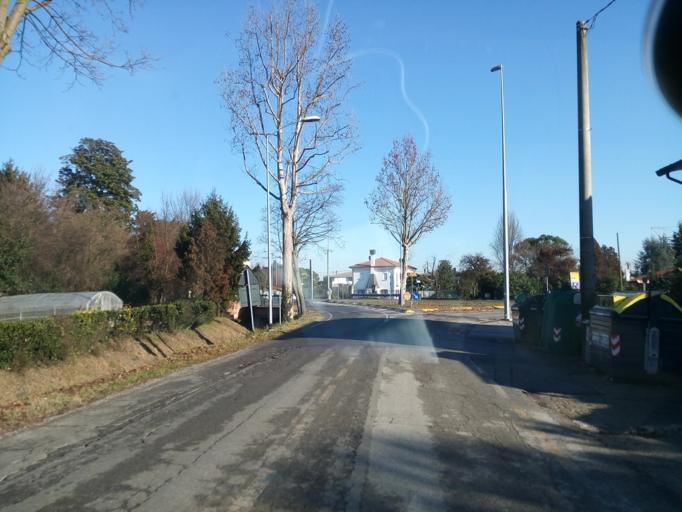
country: IT
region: Veneto
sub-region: Provincia di Venezia
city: Noale
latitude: 45.5420
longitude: 12.0686
